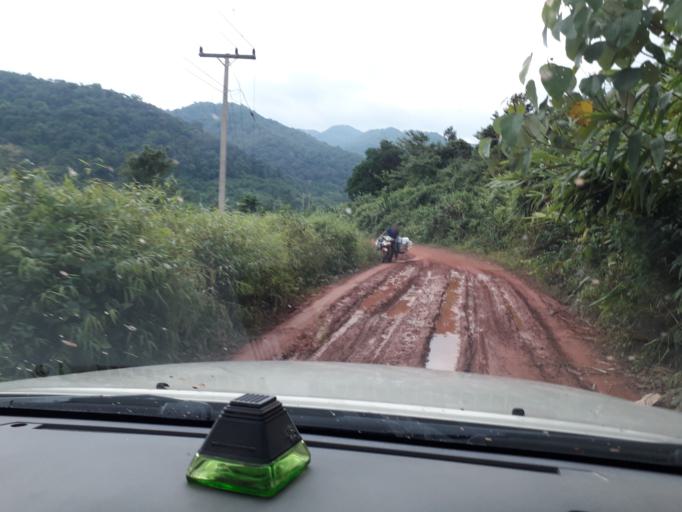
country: LA
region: Oudomxai
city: Muang La
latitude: 21.2634
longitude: 102.0033
